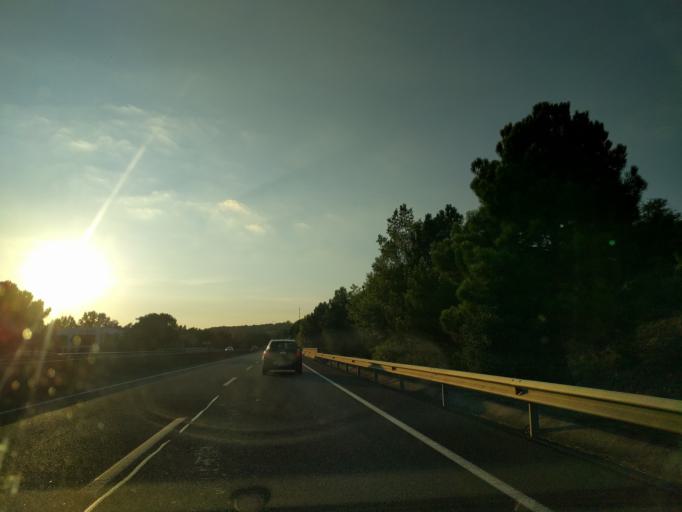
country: ES
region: Catalonia
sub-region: Provincia de Girona
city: Llagostera
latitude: 41.8273
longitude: 2.9460
